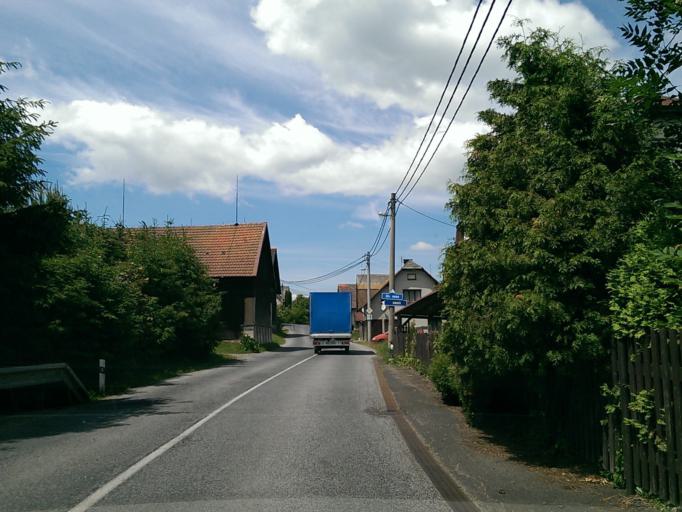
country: CZ
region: Liberecky
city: Zelezny Brod
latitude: 50.6340
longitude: 15.2792
